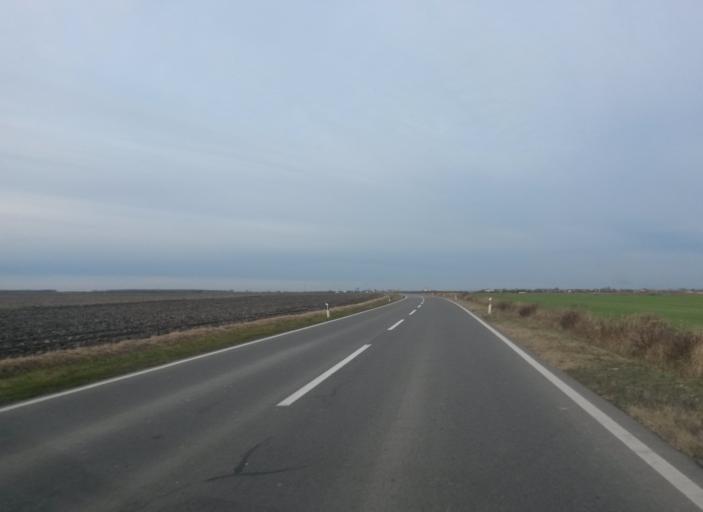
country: HR
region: Osjecko-Baranjska
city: Ovcara
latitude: 45.5015
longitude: 18.5513
